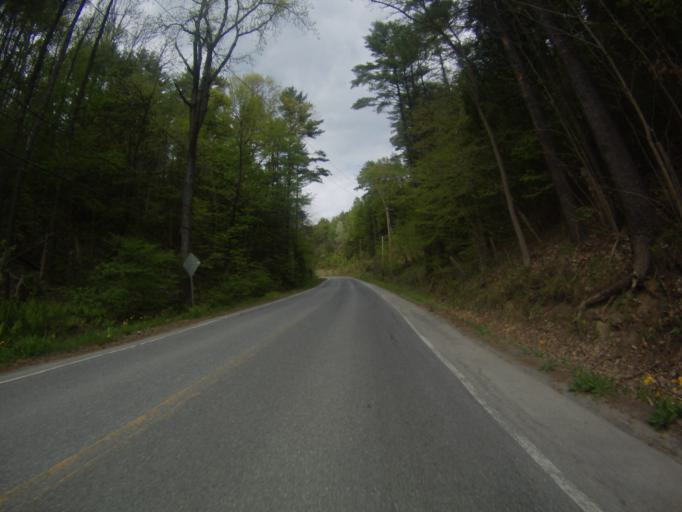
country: US
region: New York
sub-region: Essex County
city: Port Henry
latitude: 43.9451
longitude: -73.4717
